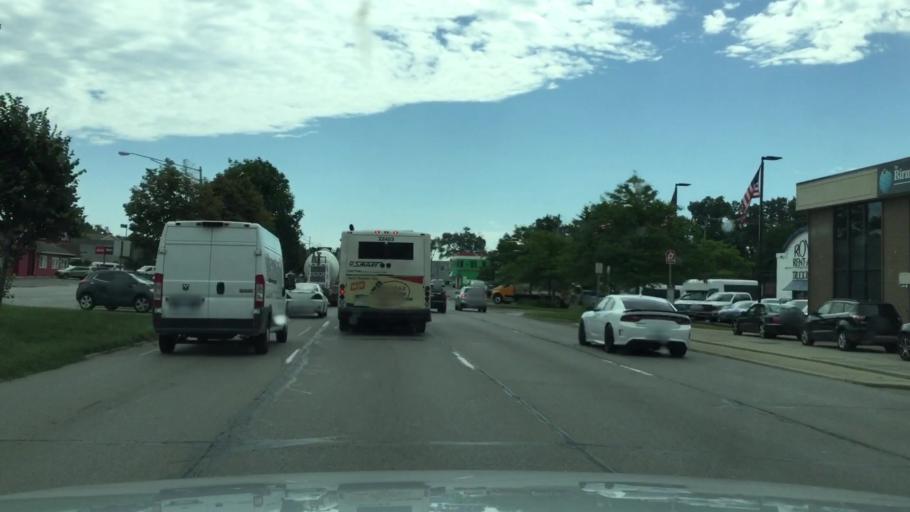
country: US
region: Michigan
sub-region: Oakland County
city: Huntington Woods
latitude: 42.4927
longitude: -83.1620
